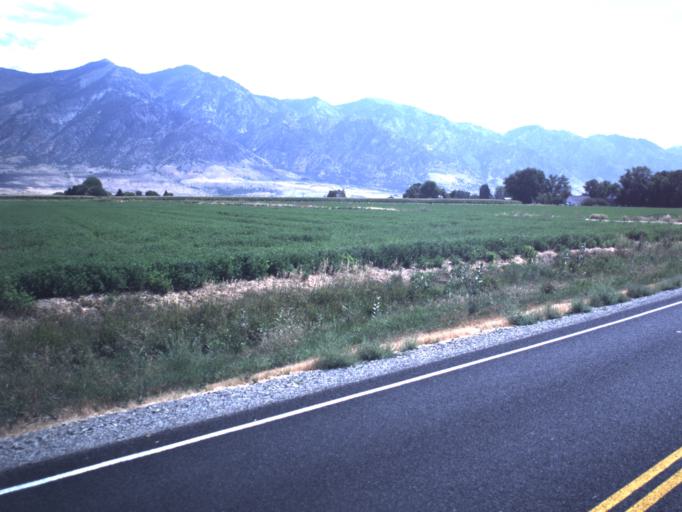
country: US
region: Utah
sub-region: Box Elder County
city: Elwood
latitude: 41.6503
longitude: -112.1386
